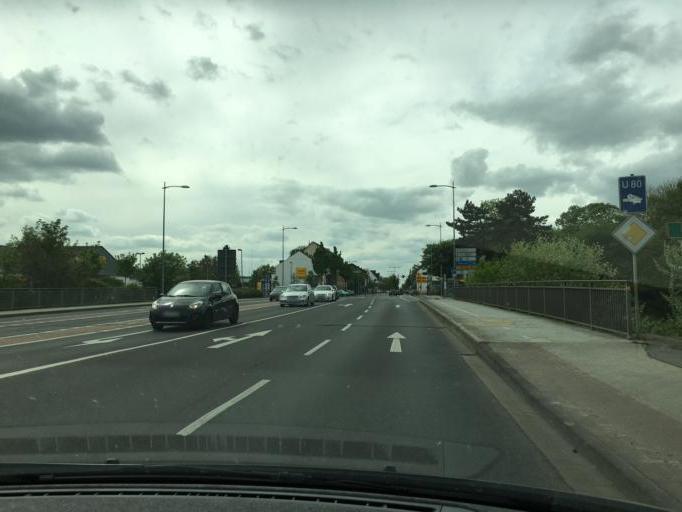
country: DE
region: North Rhine-Westphalia
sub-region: Regierungsbezirk Koln
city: Euskirchen
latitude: 50.6613
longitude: 6.8056
